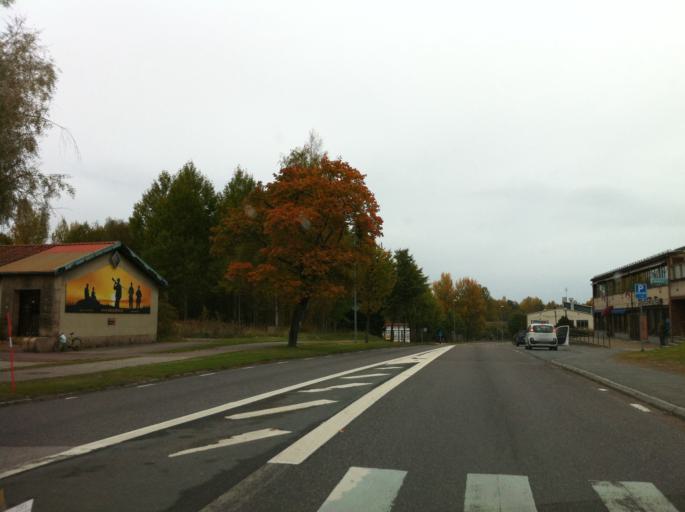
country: SE
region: Dalarna
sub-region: Ludvika Kommun
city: Grangesberg
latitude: 60.0757
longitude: 15.0064
